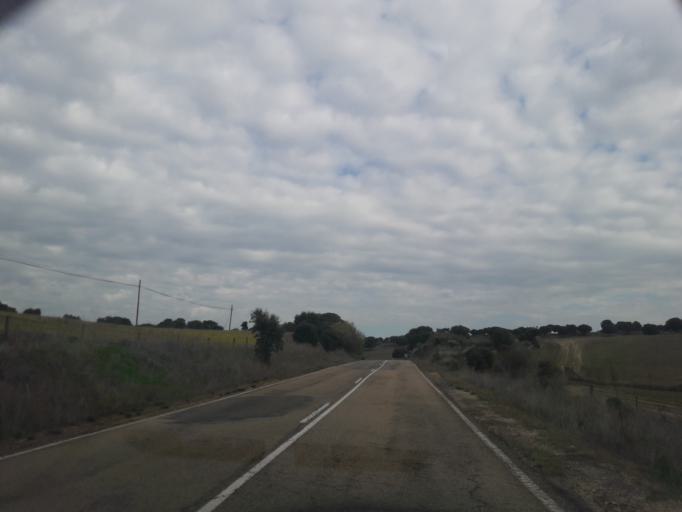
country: ES
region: Castille and Leon
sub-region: Provincia de Salamanca
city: Pastores
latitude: 40.5538
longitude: -6.5275
